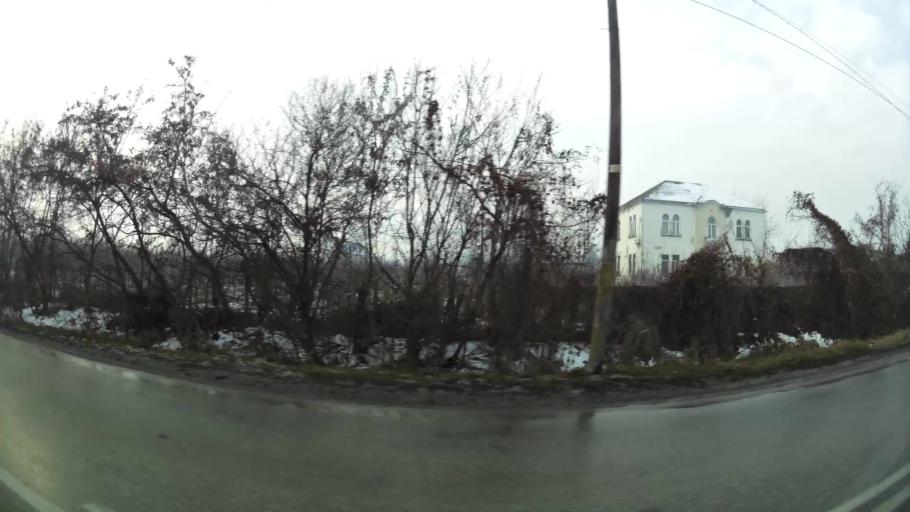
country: MK
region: Kisela Voda
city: Kisela Voda
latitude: 41.9859
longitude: 21.5189
